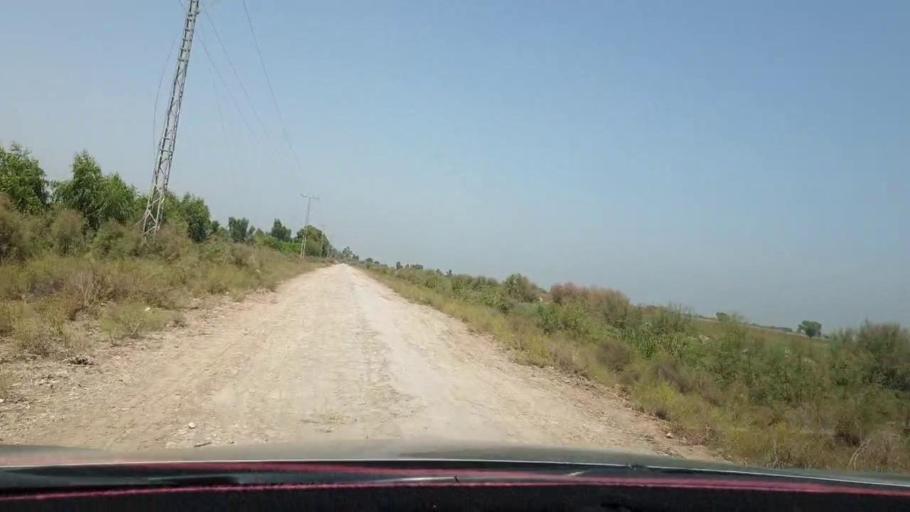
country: PK
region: Sindh
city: Warah
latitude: 27.4215
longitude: 67.6985
